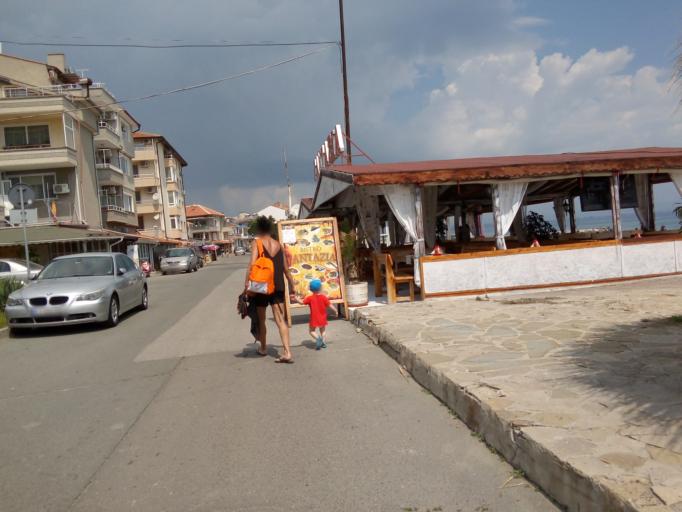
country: BG
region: Burgas
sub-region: Obshtina Pomorie
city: Pomorie
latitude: 42.5571
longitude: 27.6476
